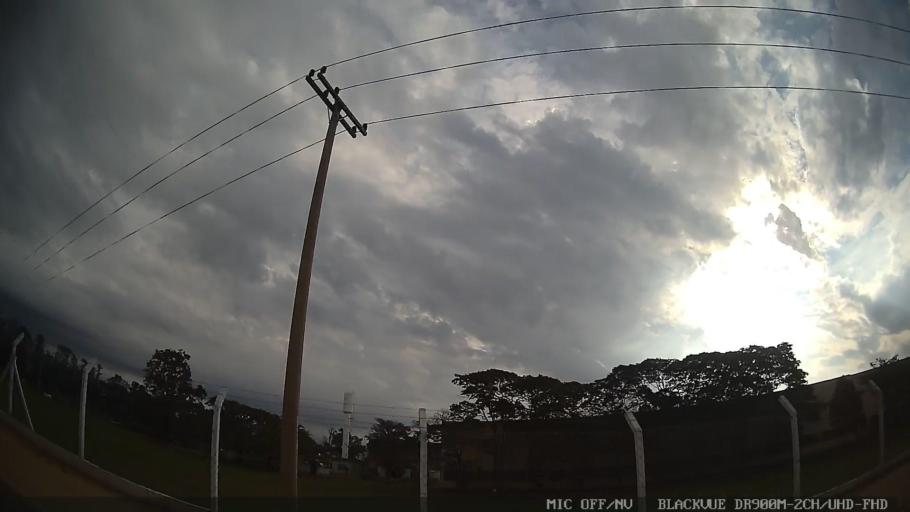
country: BR
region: Sao Paulo
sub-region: Indaiatuba
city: Indaiatuba
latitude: -23.1111
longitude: -47.2202
